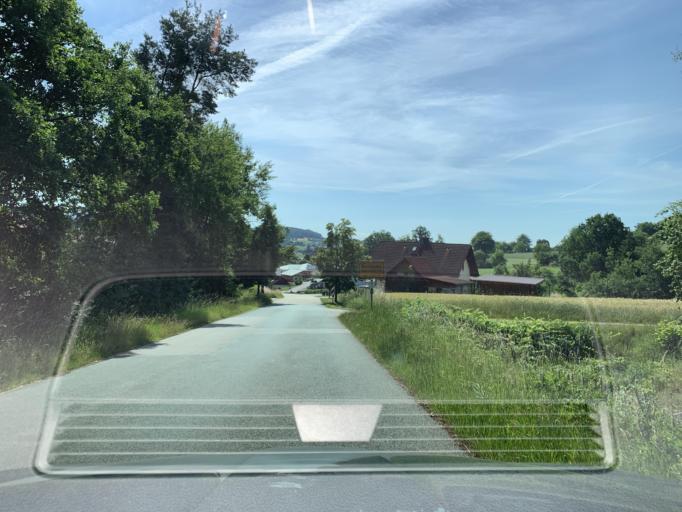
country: DE
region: Bavaria
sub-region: Upper Palatinate
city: Schwarzhofen
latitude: 49.3851
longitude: 12.3232
